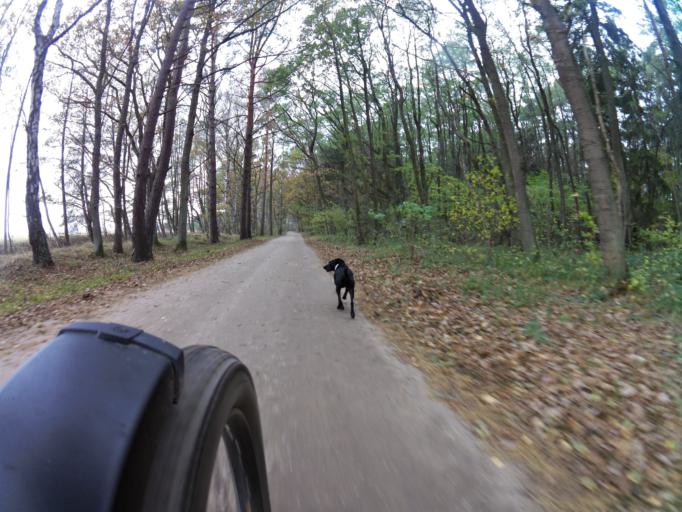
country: PL
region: Pomeranian Voivodeship
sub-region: Powiat pucki
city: Krokowa
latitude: 54.8287
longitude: 18.1224
